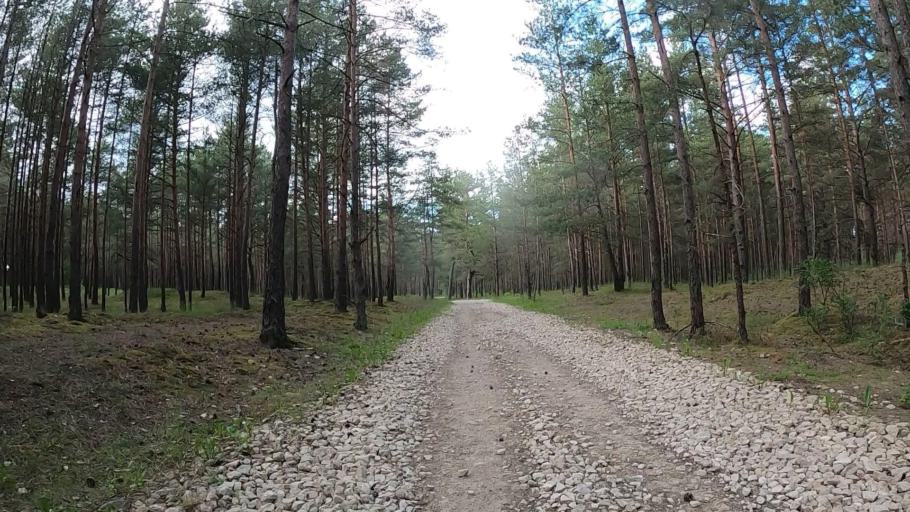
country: LV
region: Riga
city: Jaunciems
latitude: 57.0461
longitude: 24.1153
